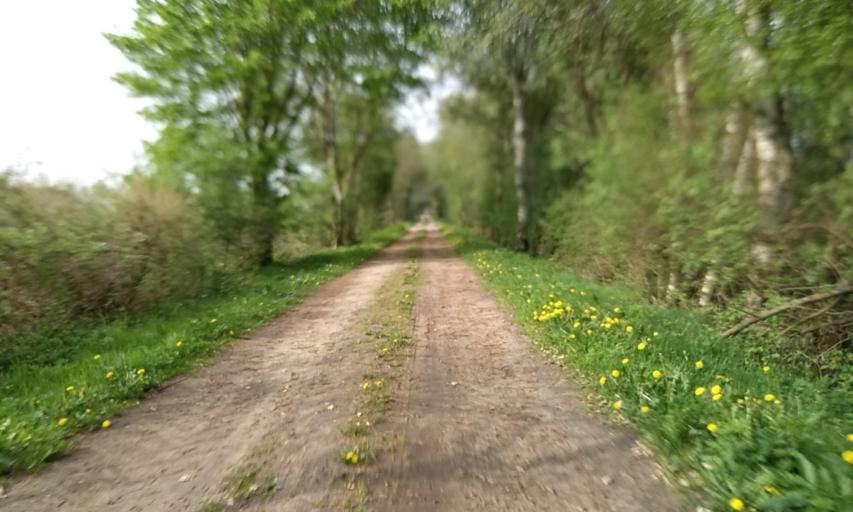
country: DE
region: Lower Saxony
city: Bliedersdorf
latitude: 53.4429
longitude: 9.5659
